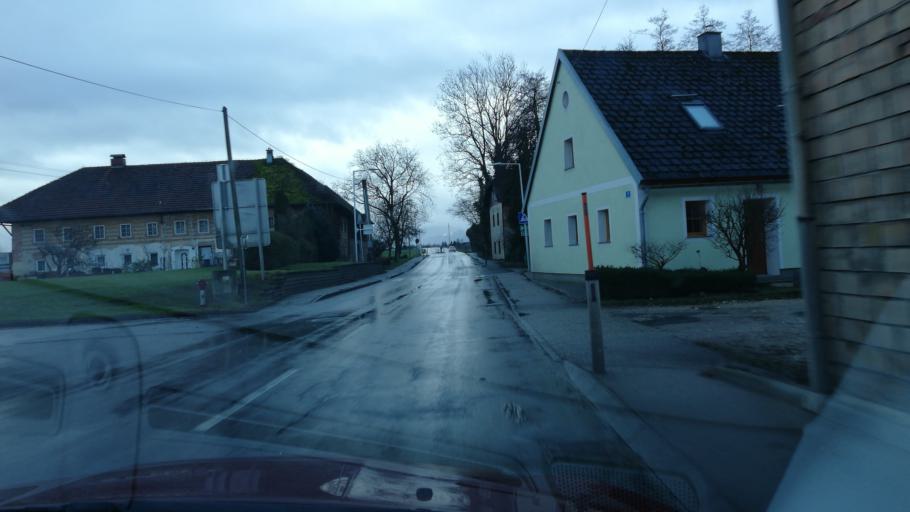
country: AT
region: Upper Austria
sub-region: Wels-Land
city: Sattledt
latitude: 48.0093
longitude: 14.0628
